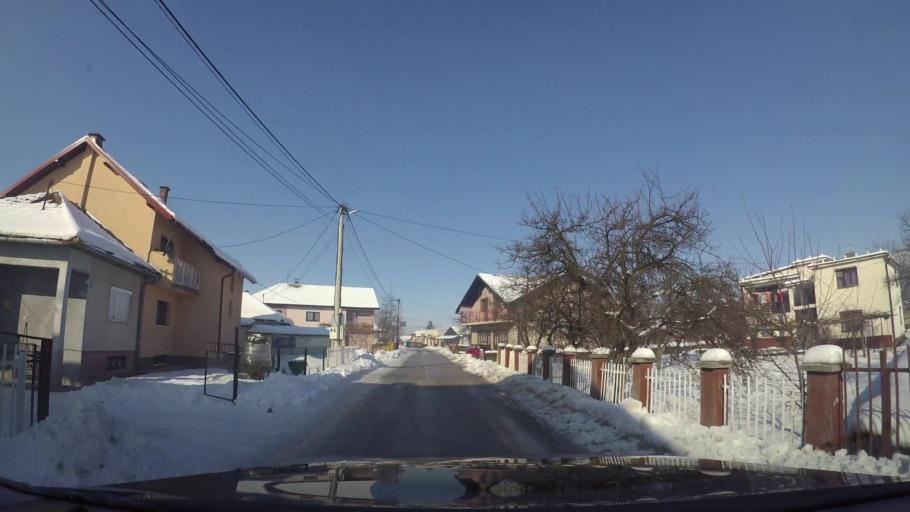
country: BA
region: Federation of Bosnia and Herzegovina
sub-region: Kanton Sarajevo
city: Sarajevo
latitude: 43.7951
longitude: 18.3488
